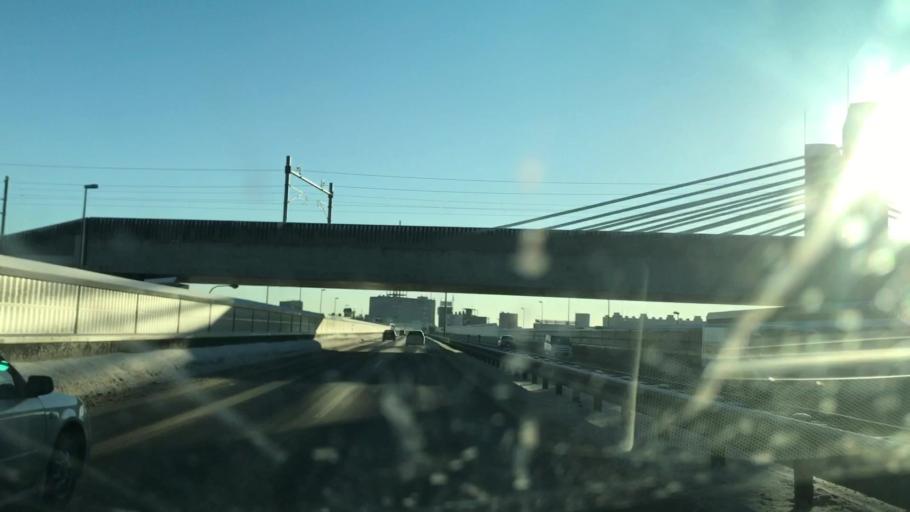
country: JP
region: Hokkaido
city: Sapporo
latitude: 43.1017
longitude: 141.3254
